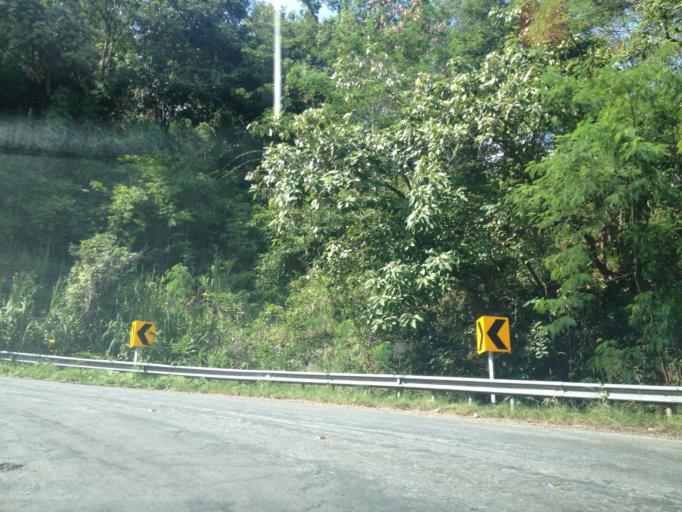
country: TH
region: Chiang Mai
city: Samoeng
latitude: 18.8073
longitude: 98.8114
